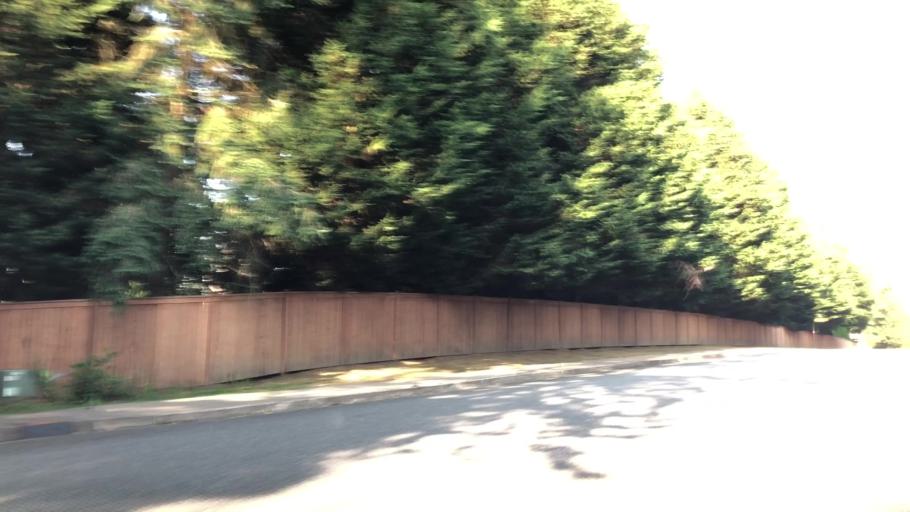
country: US
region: Washington
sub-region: King County
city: Cottage Lake
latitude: 47.7217
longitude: -122.0996
